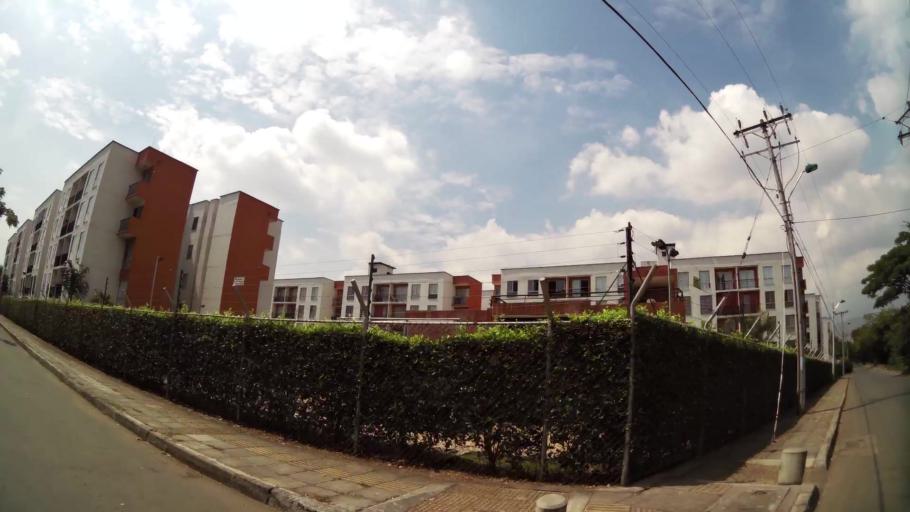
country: CO
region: Valle del Cauca
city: Cali
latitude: 3.4974
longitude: -76.4995
